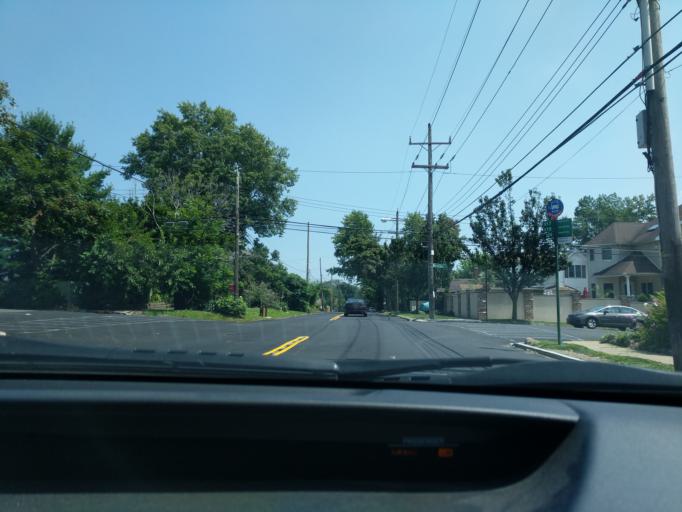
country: US
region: New York
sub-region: Richmond County
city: Staten Island
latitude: 40.5486
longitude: -74.1846
